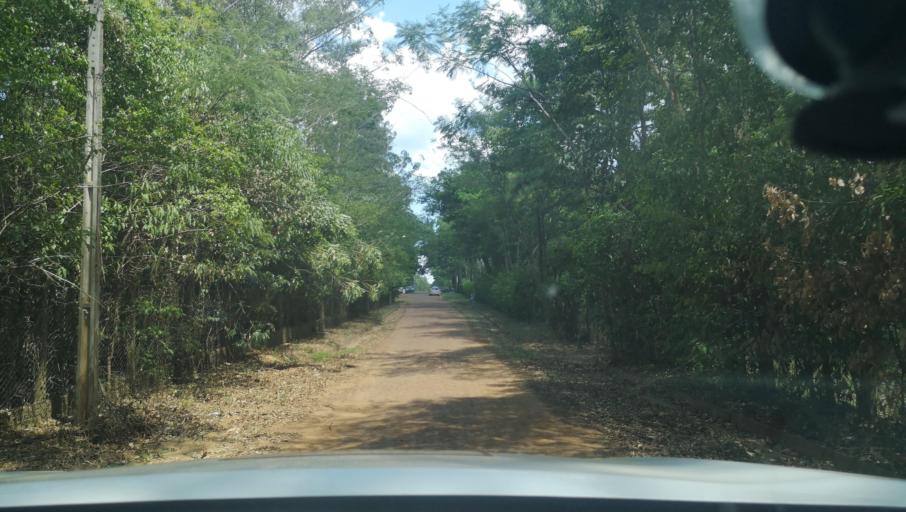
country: PY
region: Itapua
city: Carmen del Parana
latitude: -27.1513
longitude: -56.2480
